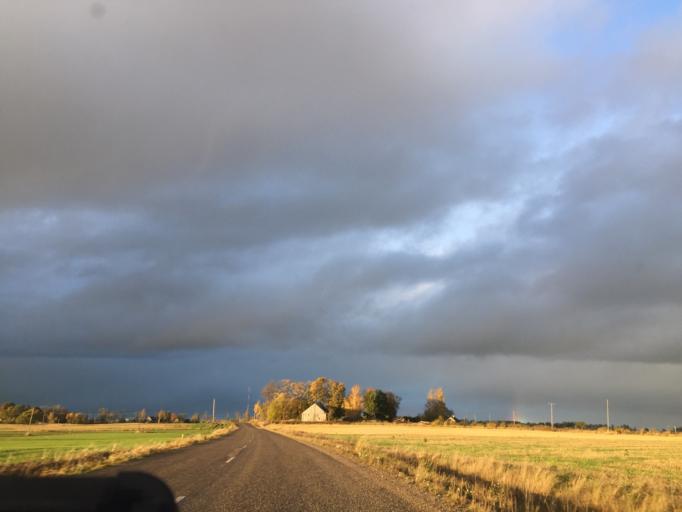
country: LV
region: Talsu Rajons
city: Sabile
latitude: 56.9325
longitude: 22.3973
